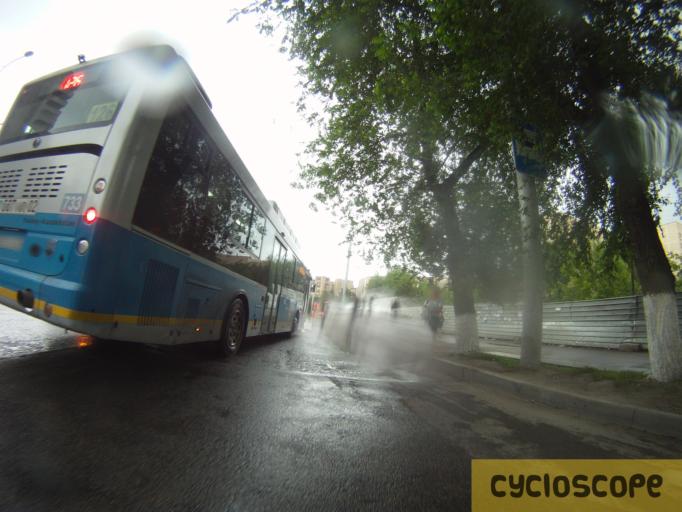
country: KZ
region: Almaty Qalasy
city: Almaty
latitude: 43.2399
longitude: 76.8334
